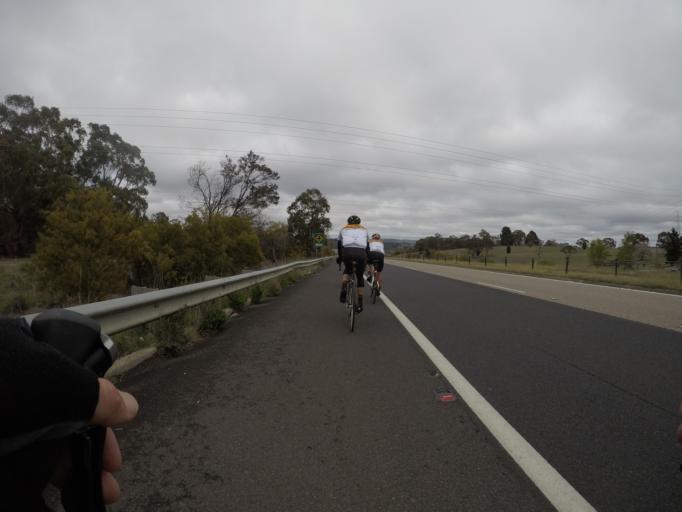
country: AU
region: New South Wales
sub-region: Lithgow
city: Lithgow
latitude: -33.4268
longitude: 150.0960
